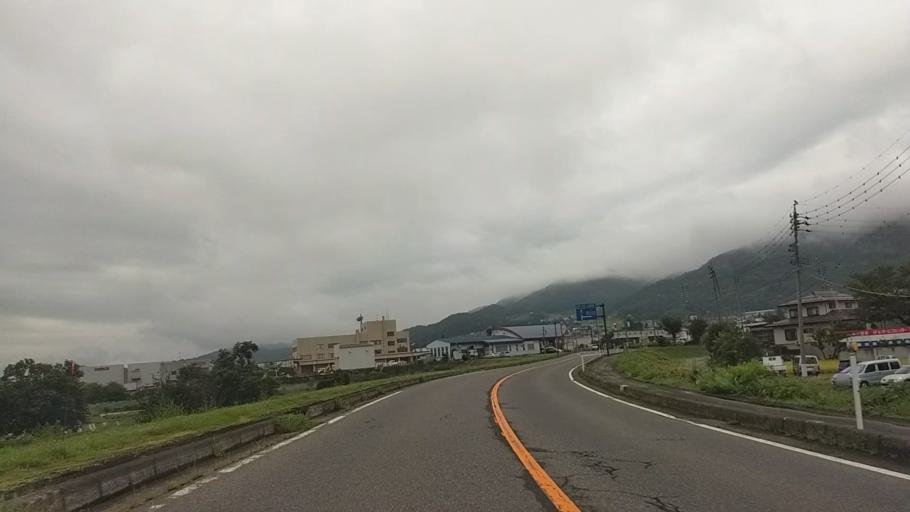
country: JP
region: Nagano
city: Iiyama
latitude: 36.8389
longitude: 138.3611
